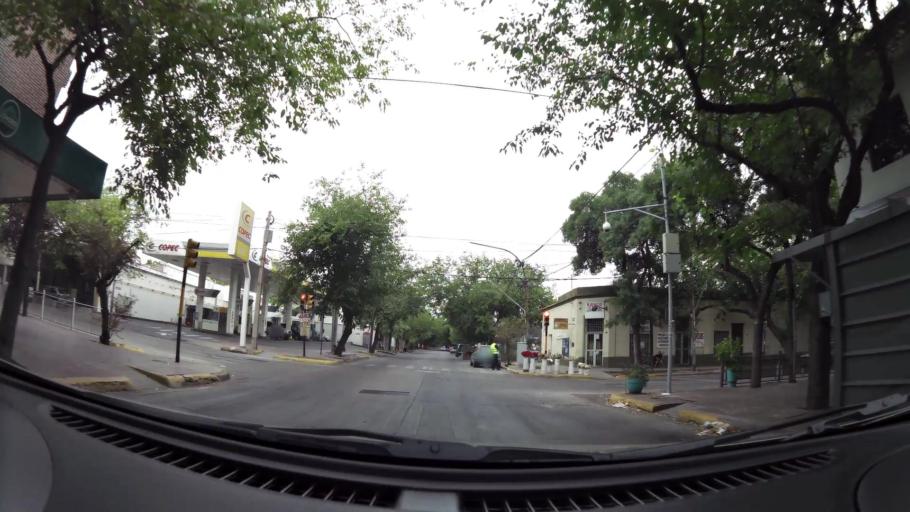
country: AR
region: Mendoza
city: Mendoza
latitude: -32.8758
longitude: -68.8555
